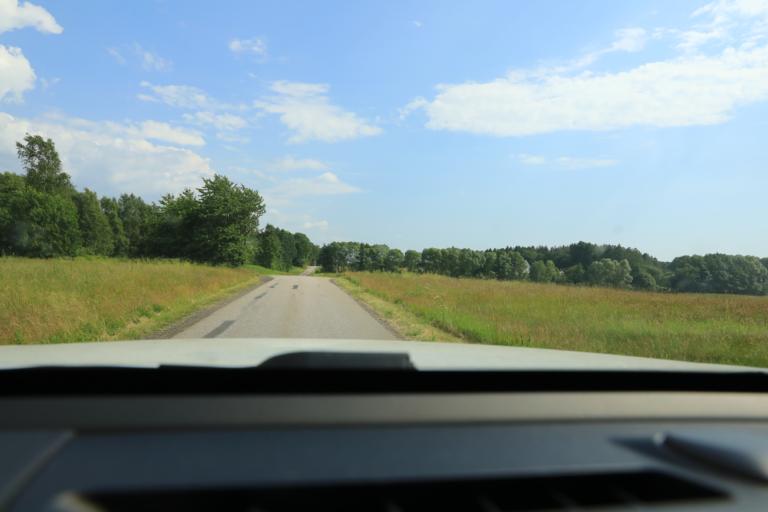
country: SE
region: Halland
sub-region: Varbergs Kommun
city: Varberg
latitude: 57.1564
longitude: 12.3174
